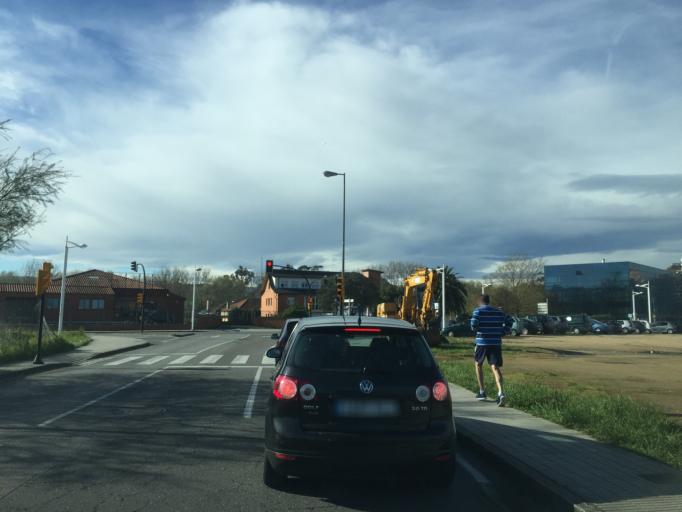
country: ES
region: Asturias
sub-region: Province of Asturias
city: Gijon
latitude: 43.5424
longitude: -5.6420
